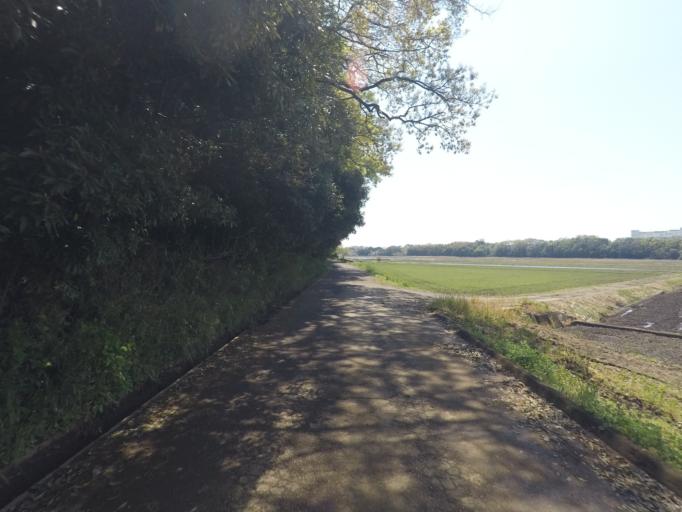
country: JP
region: Ibaraki
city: Ushiku
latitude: 35.9988
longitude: 140.1020
